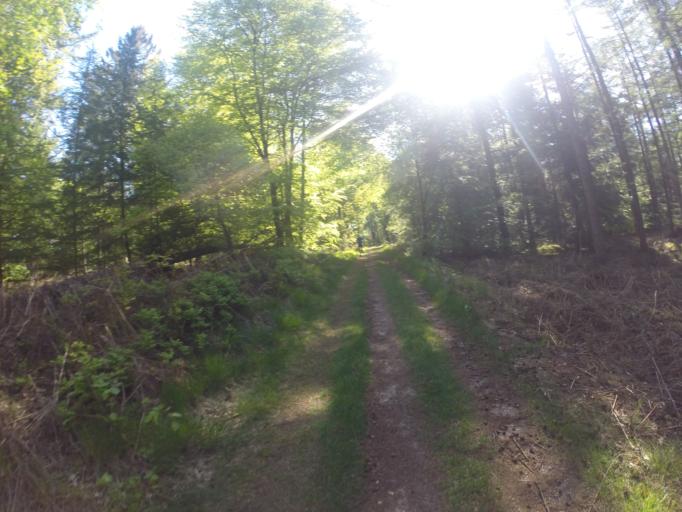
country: NL
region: Gelderland
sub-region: Gemeente Montferland
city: s-Heerenberg
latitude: 51.9125
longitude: 6.2242
